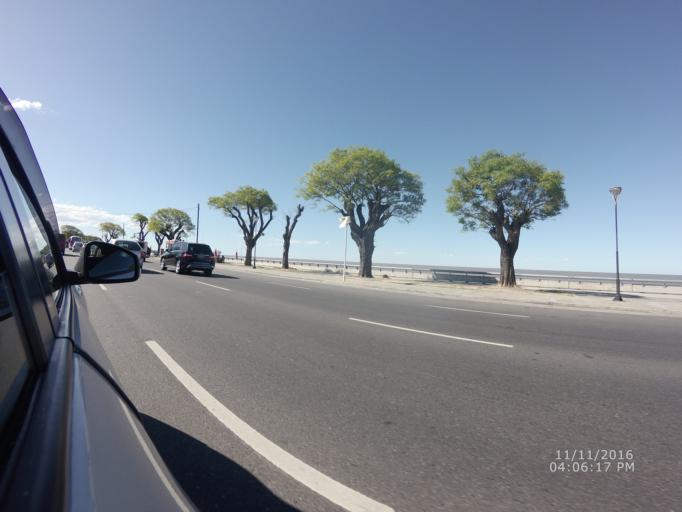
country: AR
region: Buenos Aires F.D.
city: Retiro
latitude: -34.5609
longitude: -58.4073
